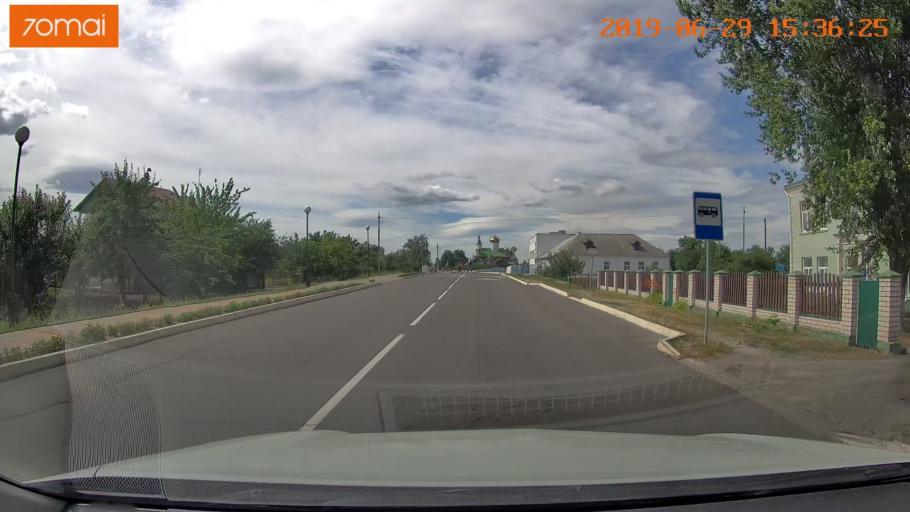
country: BY
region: Brest
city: Mikashevichy
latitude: 52.2205
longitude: 27.4683
